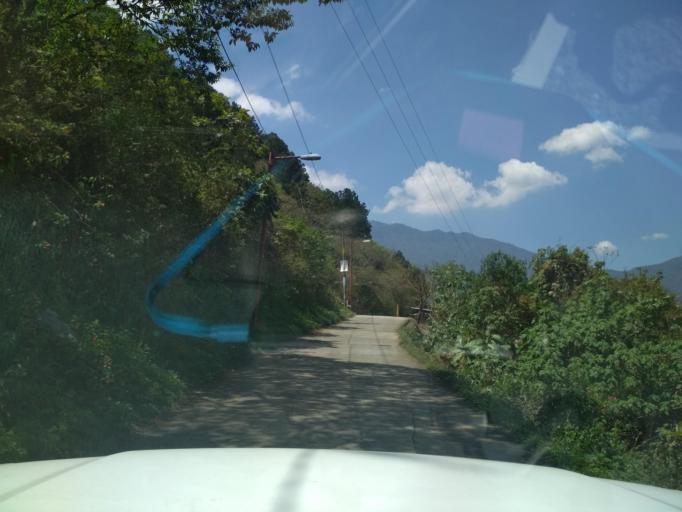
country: MX
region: Veracruz
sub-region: Tlilapan
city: Tonalixco
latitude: 18.7829
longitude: -97.0847
